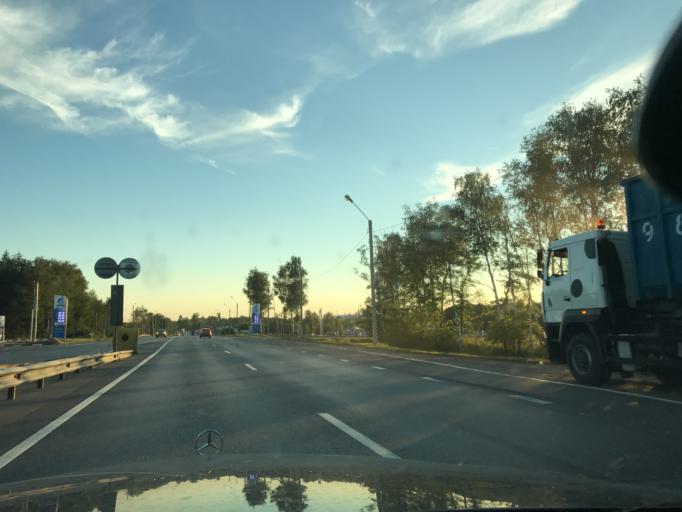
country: RU
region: Vladimir
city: Lakinsk
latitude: 55.9683
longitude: 39.7874
